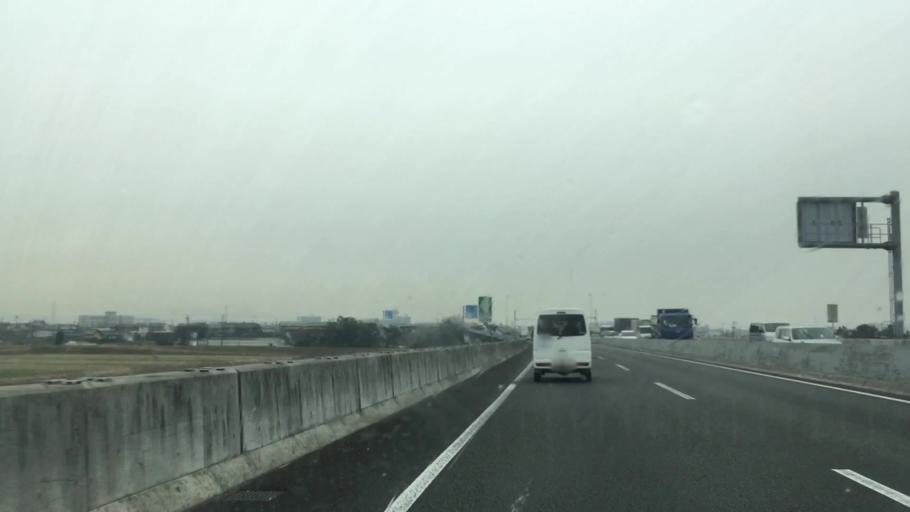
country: JP
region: Aichi
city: Anjo
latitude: 34.9373
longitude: 137.0421
